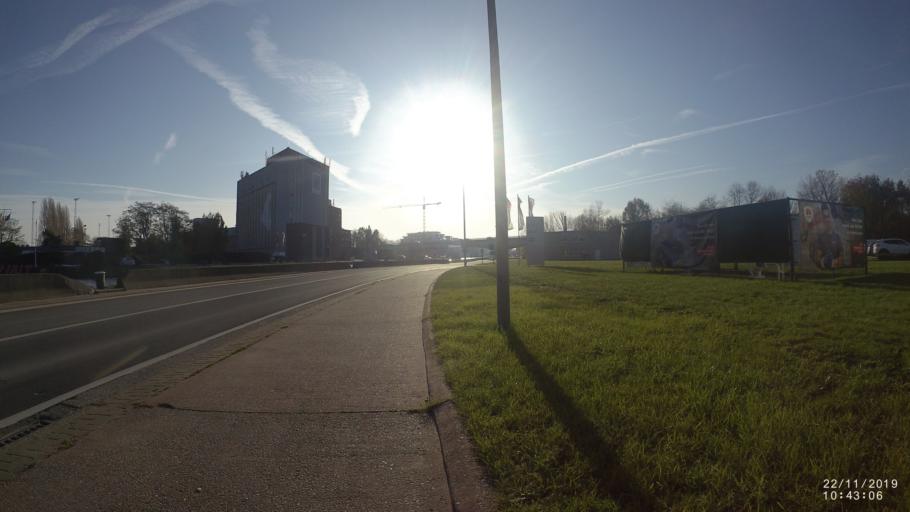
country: BE
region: Flanders
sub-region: Provincie Limburg
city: Hasselt
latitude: 50.9439
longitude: 5.3332
